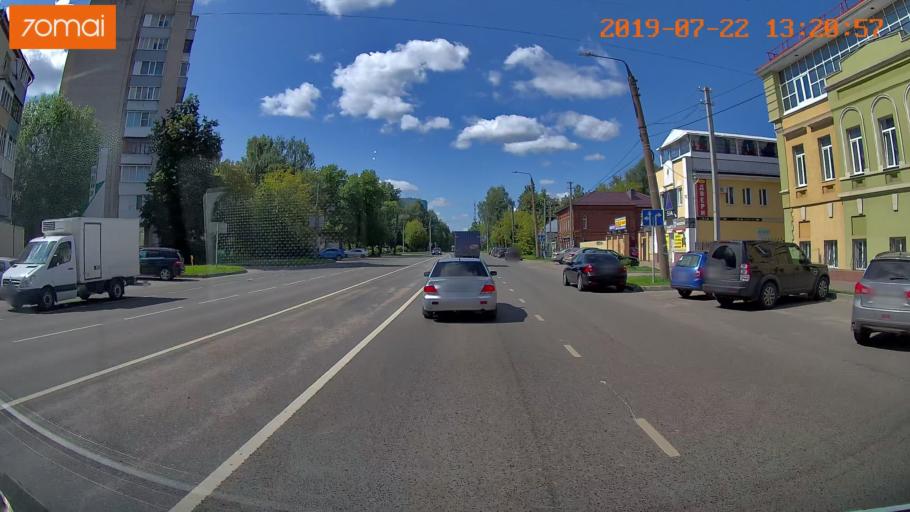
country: RU
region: Ivanovo
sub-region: Gorod Ivanovo
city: Ivanovo
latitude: 57.0213
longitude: 40.9673
